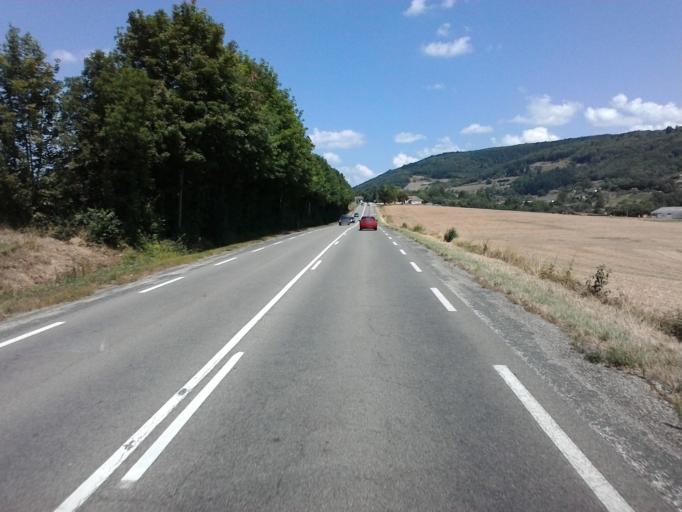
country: FR
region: Rhone-Alpes
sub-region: Departement de l'Ain
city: Coligny
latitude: 46.3725
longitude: 5.3403
